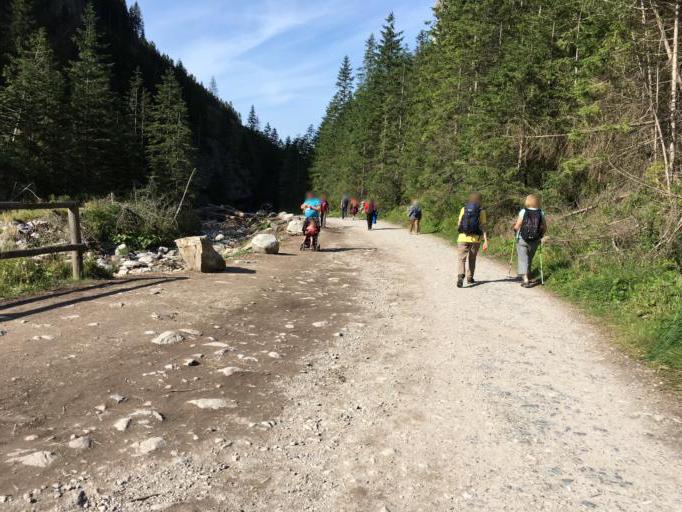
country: PL
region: Lesser Poland Voivodeship
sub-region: Powiat tatrzanski
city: Koscielisko
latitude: 49.2454
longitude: 19.8128
